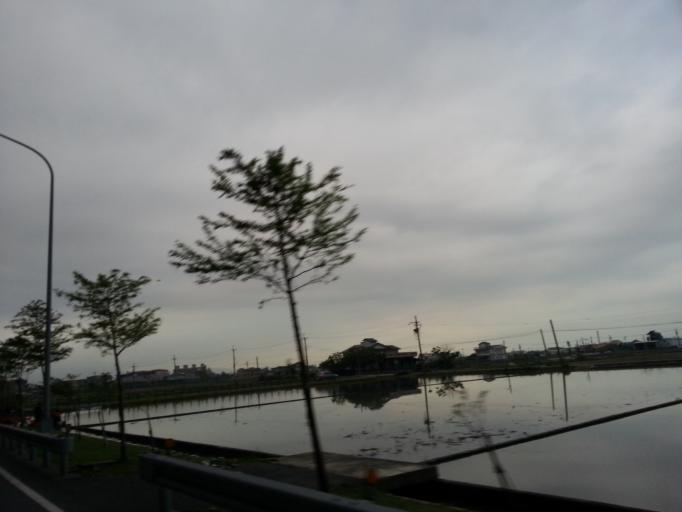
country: TW
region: Taiwan
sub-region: Yilan
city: Yilan
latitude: 24.6359
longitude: 121.8061
